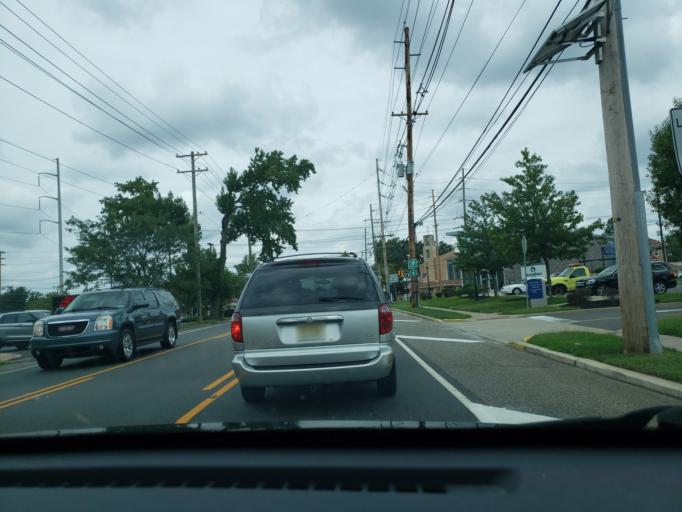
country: US
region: New Jersey
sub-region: Camden County
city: Glendora
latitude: 39.8436
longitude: -75.0707
